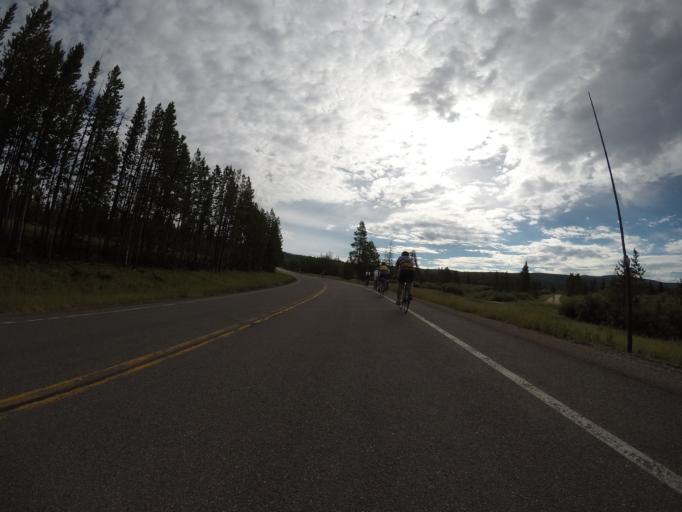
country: US
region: Wyoming
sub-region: Carbon County
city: Saratoga
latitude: 41.3240
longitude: -106.5025
